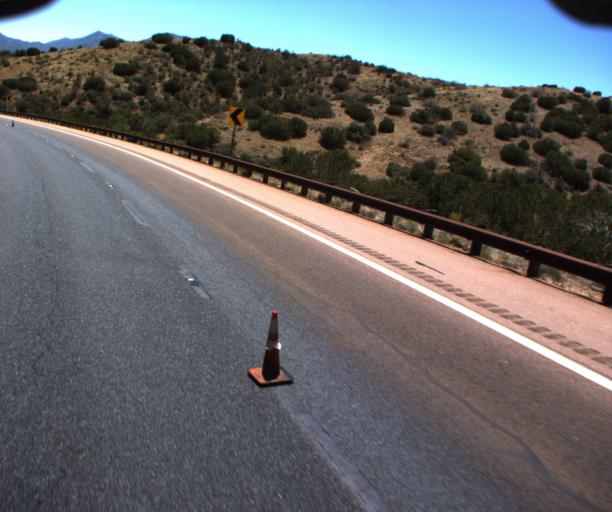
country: US
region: Arizona
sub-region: Gila County
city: Payson
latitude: 34.1566
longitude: -111.3383
